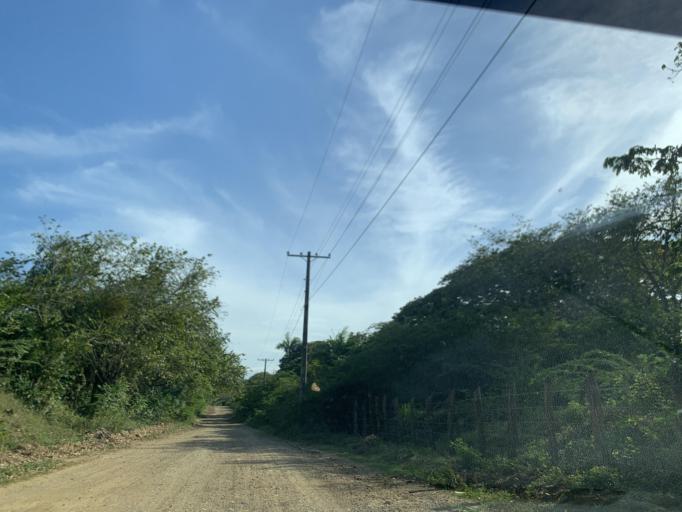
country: DO
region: Puerto Plata
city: Luperon
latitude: 19.8821
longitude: -70.9247
